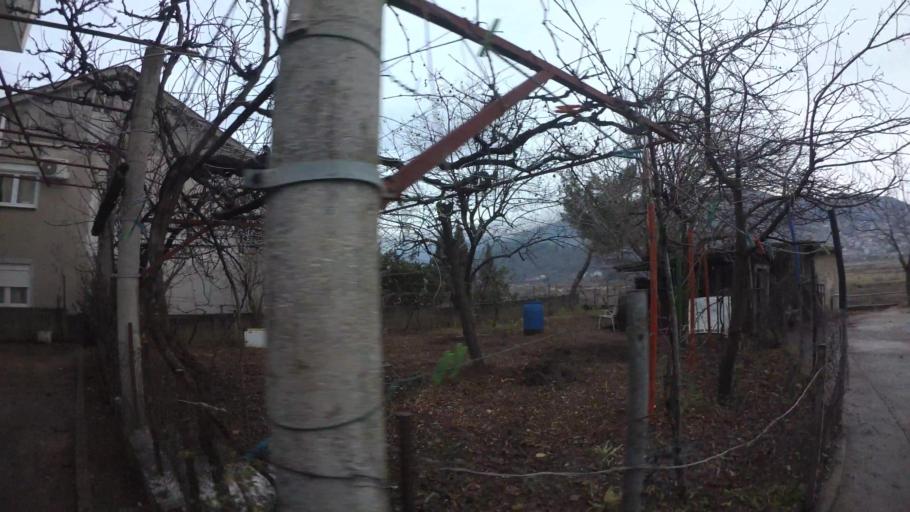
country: BA
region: Federation of Bosnia and Herzegovina
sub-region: Hercegovacko-Bosanski Kanton
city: Mostar
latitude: 43.3648
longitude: 17.8075
